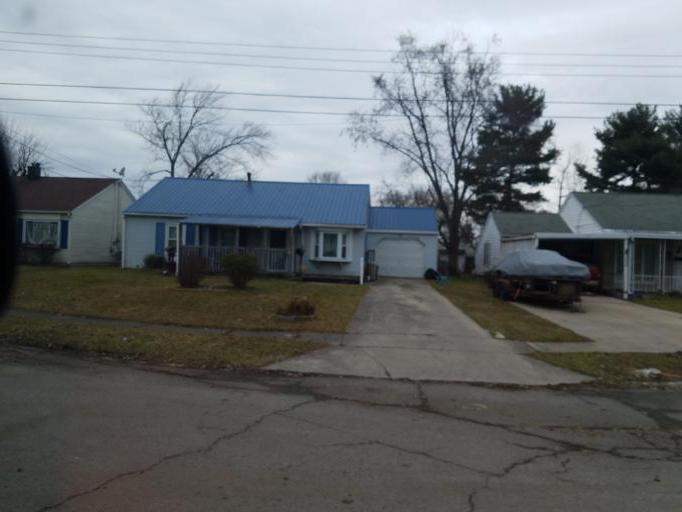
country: US
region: Ohio
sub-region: Marion County
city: Marion
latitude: 40.6046
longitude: -83.1172
